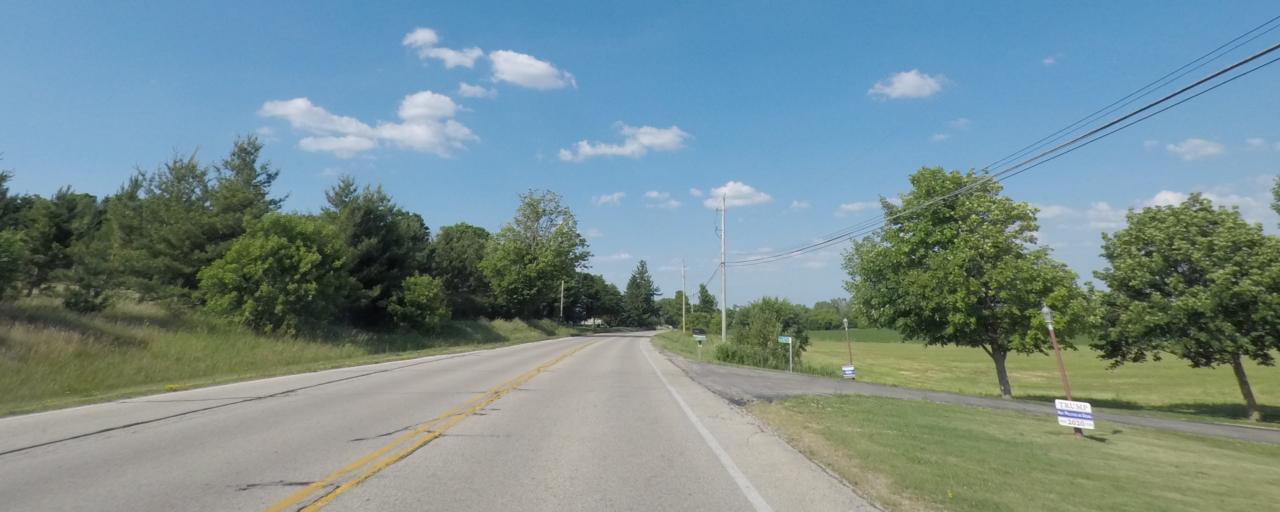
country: US
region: Wisconsin
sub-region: Waukesha County
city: Big Bend
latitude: 42.8461
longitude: -88.2622
